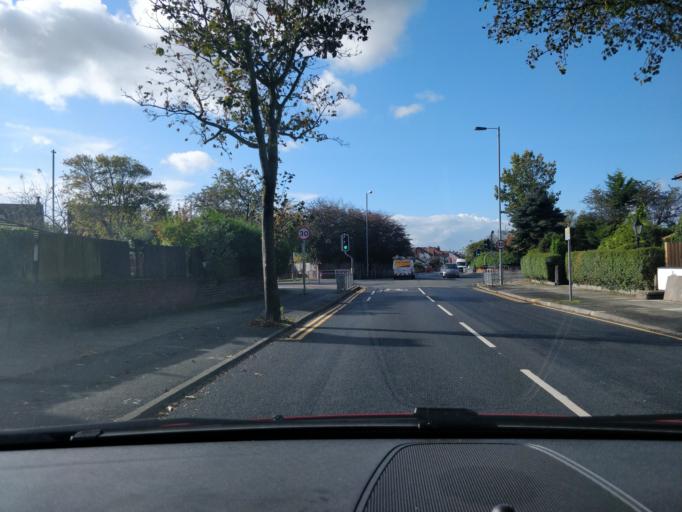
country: GB
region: England
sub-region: Sefton
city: Southport
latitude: 53.6373
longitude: -2.9824
